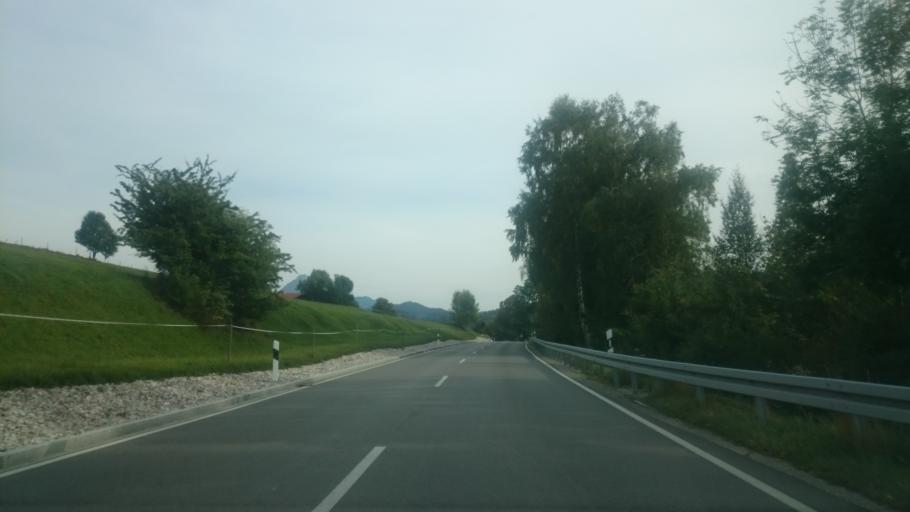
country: AT
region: Tyrol
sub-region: Politischer Bezirk Reutte
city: Vils
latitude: 47.5756
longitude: 10.6343
